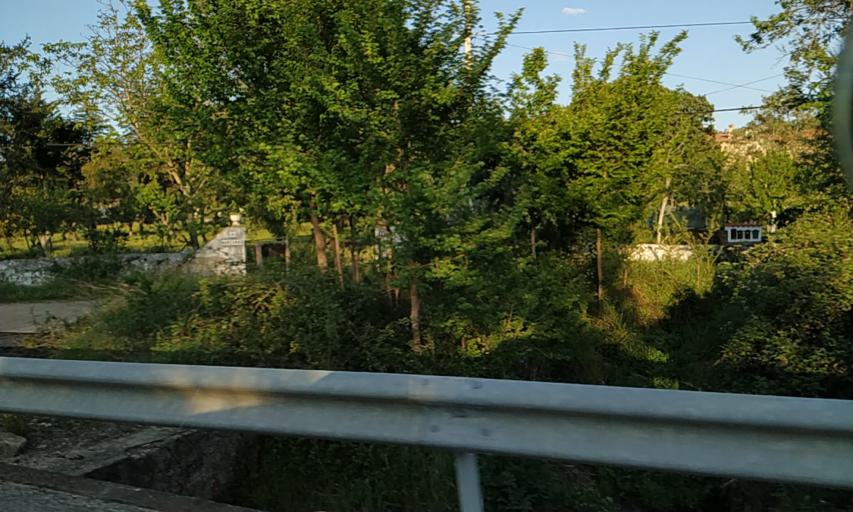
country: ES
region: Extremadura
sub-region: Provincia de Caceres
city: Valencia de Alcantara
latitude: 39.3635
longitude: -7.2725
